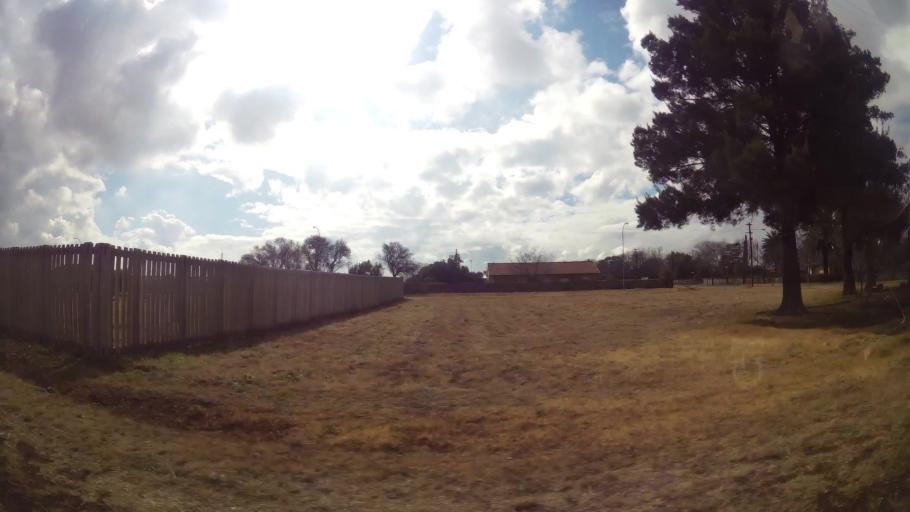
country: ZA
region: Gauteng
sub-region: Sedibeng District Municipality
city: Meyerton
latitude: -26.6148
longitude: 28.0523
